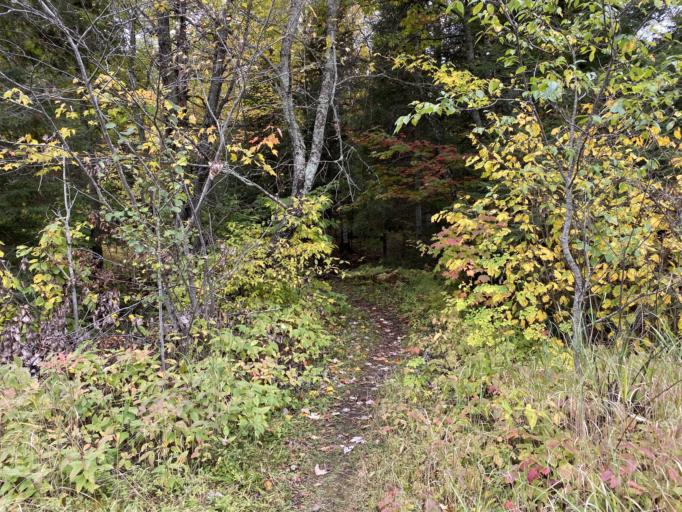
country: US
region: Michigan
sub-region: Marquette County
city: West Ishpeming
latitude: 46.5370
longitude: -88.0006
